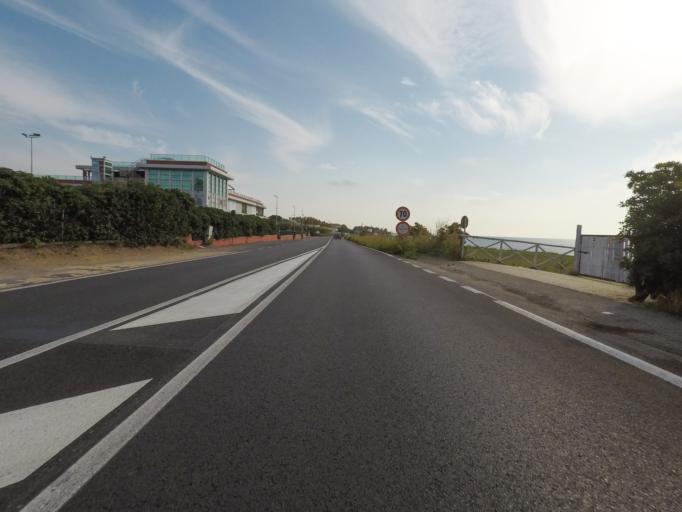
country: IT
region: Latium
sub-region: Citta metropolitana di Roma Capitale
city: Civitavecchia
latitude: 42.0542
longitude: 11.8201
